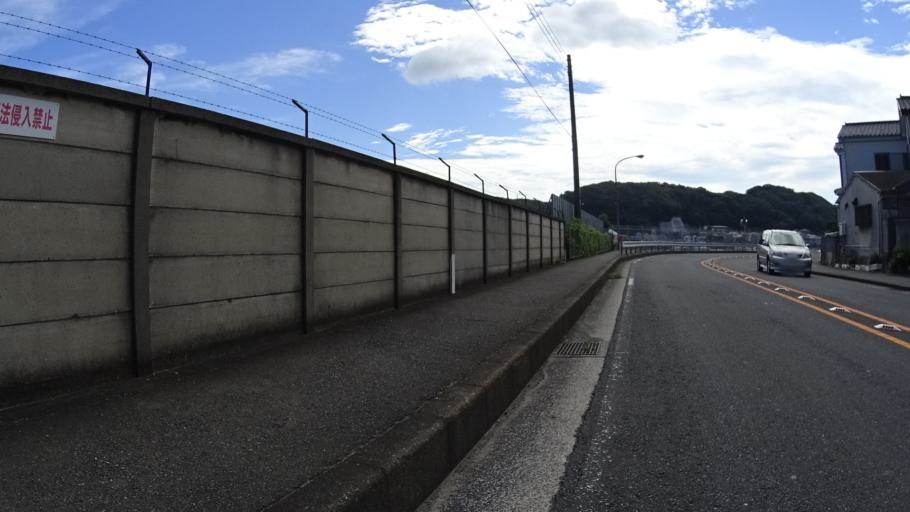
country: JP
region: Kanagawa
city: Yokosuka
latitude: 35.2446
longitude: 139.7169
